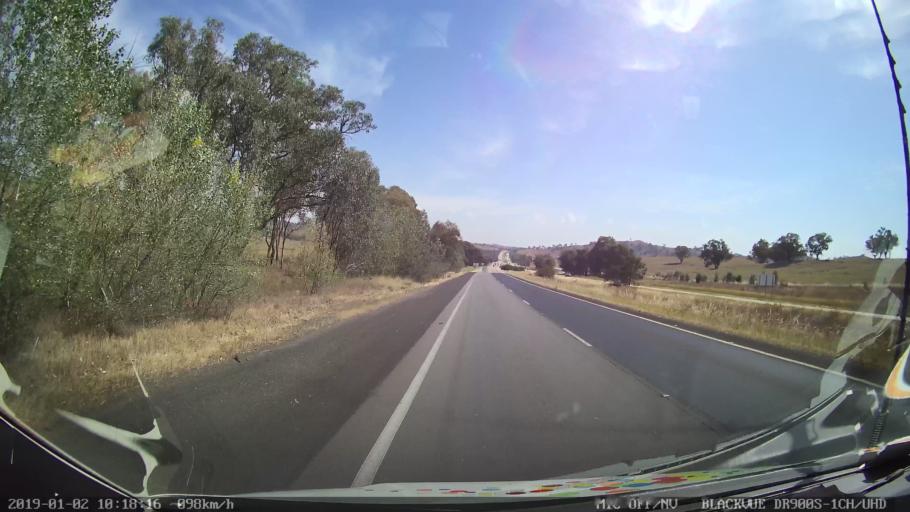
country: AU
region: New South Wales
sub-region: Gundagai
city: Gundagai
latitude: -35.0126
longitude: 148.1102
